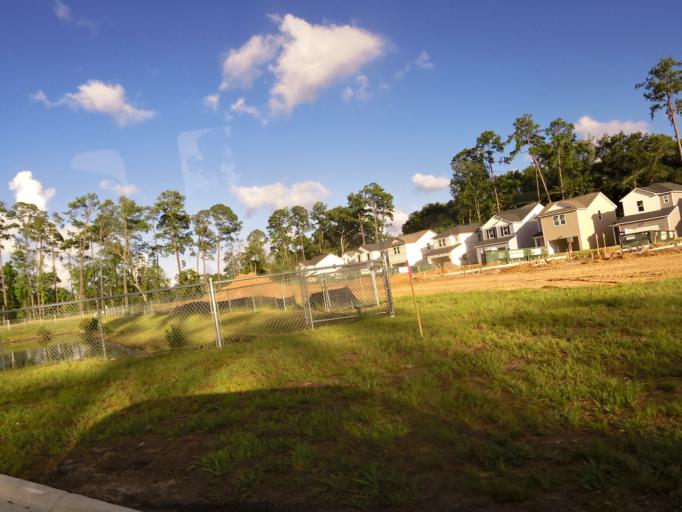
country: US
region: Florida
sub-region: Duval County
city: Jacksonville
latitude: 30.4231
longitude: -81.6933
